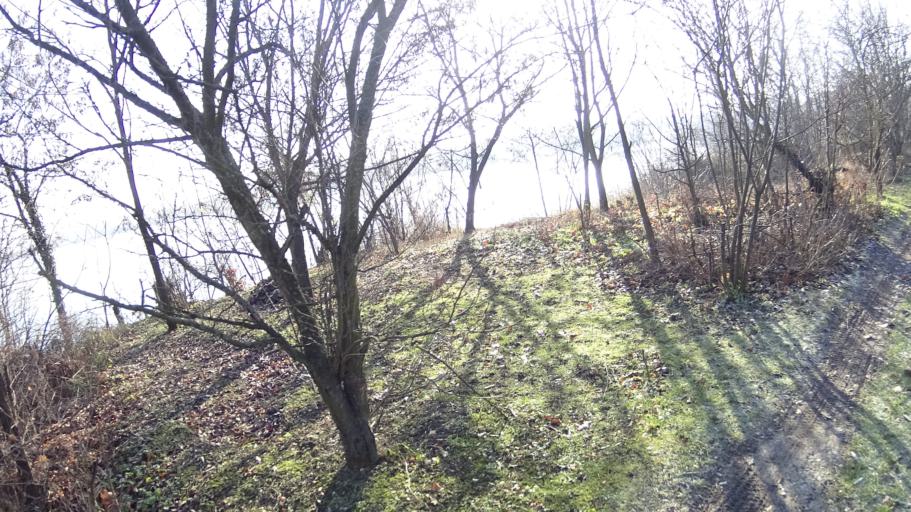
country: HU
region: Borsod-Abauj-Zemplen
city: Nyekladhaza
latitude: 47.9875
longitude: 20.8564
